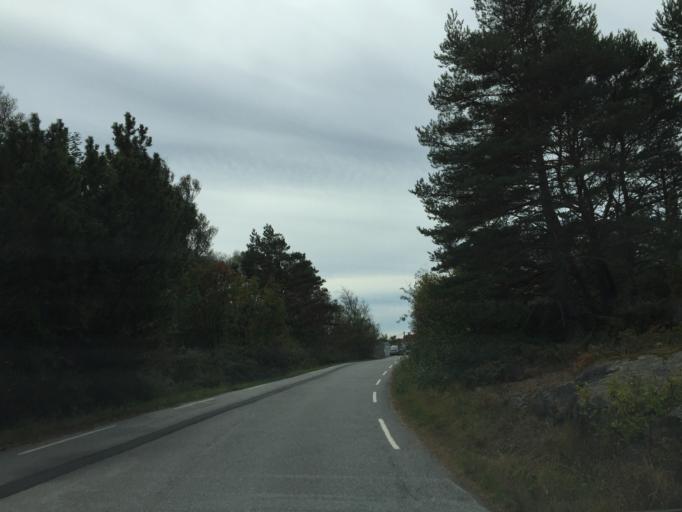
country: NO
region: Ostfold
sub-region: Hvaler
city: Skjaerhalden
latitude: 59.0454
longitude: 10.9541
